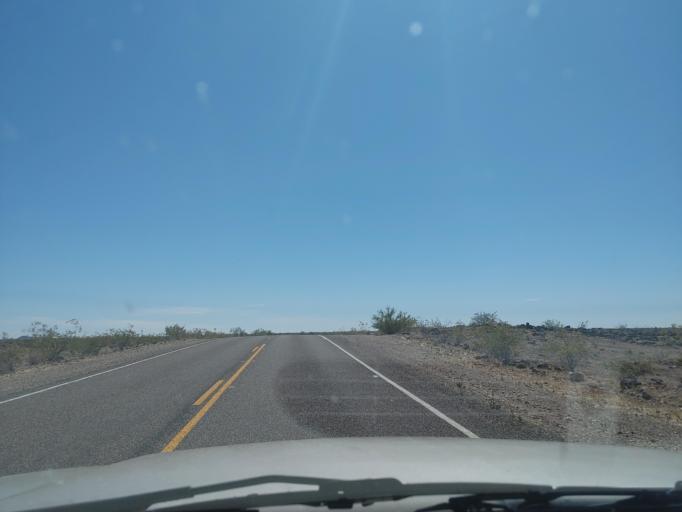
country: US
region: Arizona
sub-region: Maricopa County
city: Gila Bend
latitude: 32.9185
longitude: -113.2827
